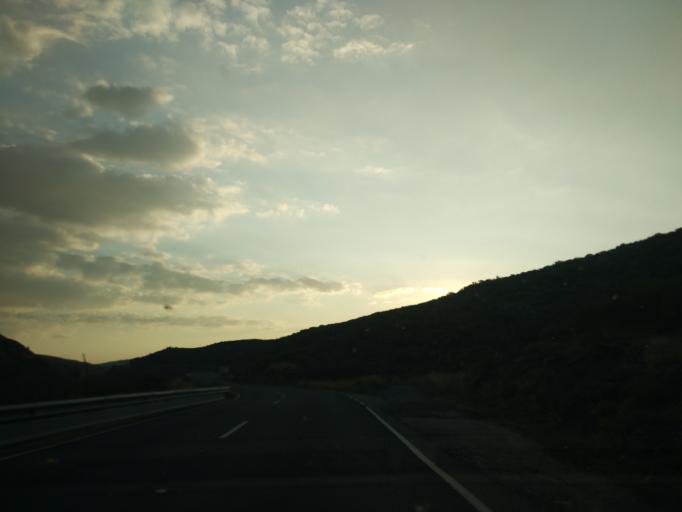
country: ES
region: Castille and Leon
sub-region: Provincia de Avila
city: San Martin del Pimpollar
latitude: 40.3728
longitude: -5.0297
